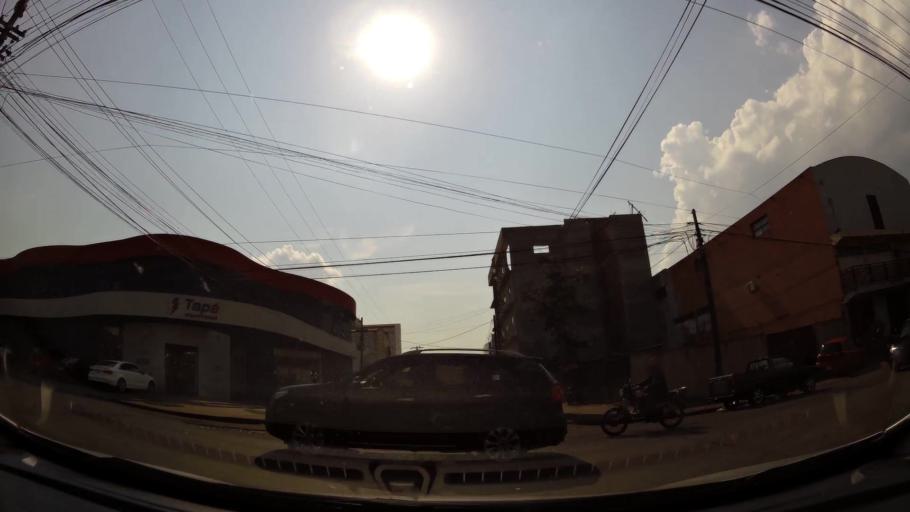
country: PY
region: Alto Parana
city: Ciudad del Este
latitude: -25.5052
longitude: -54.6354
